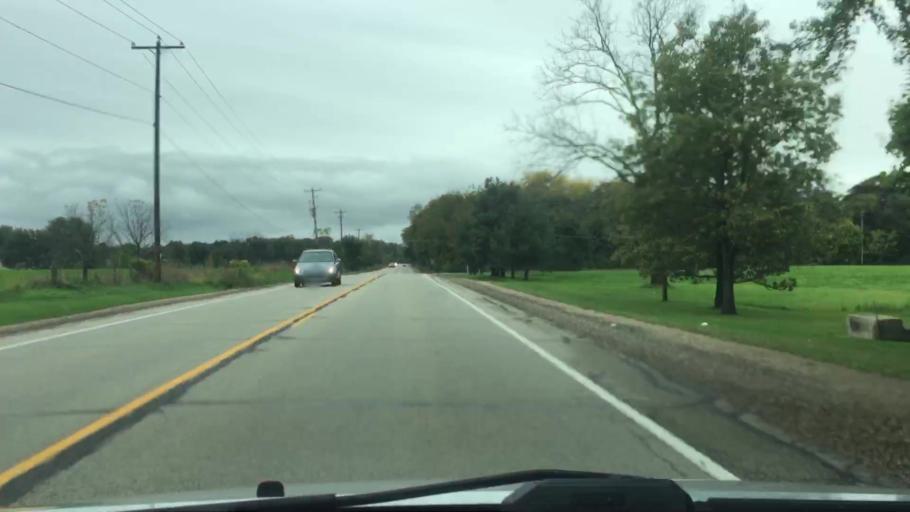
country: US
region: Wisconsin
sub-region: Walworth County
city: Elkhorn
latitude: 42.7762
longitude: -88.5546
